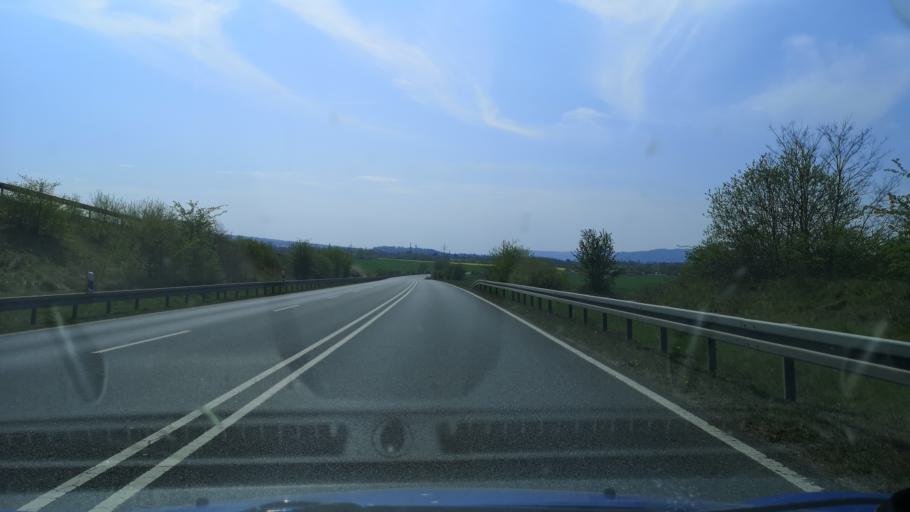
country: DE
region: Lower Saxony
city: Bevern
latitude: 51.8453
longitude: 9.4921
